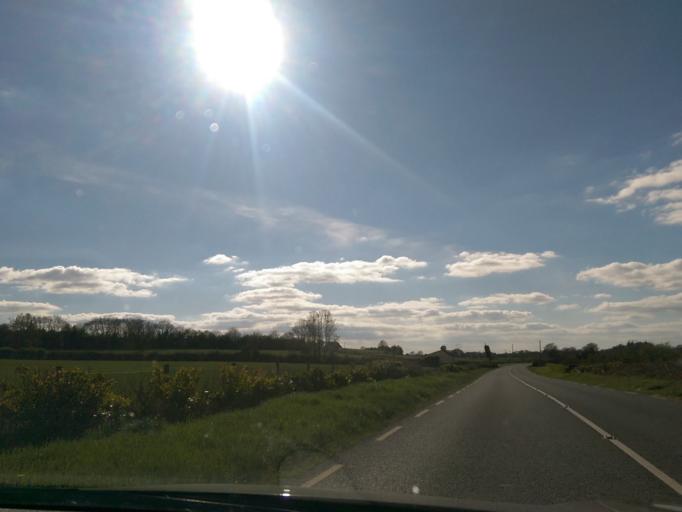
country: IE
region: Leinster
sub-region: Uibh Fhaili
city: Banagher
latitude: 53.1061
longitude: -8.0292
